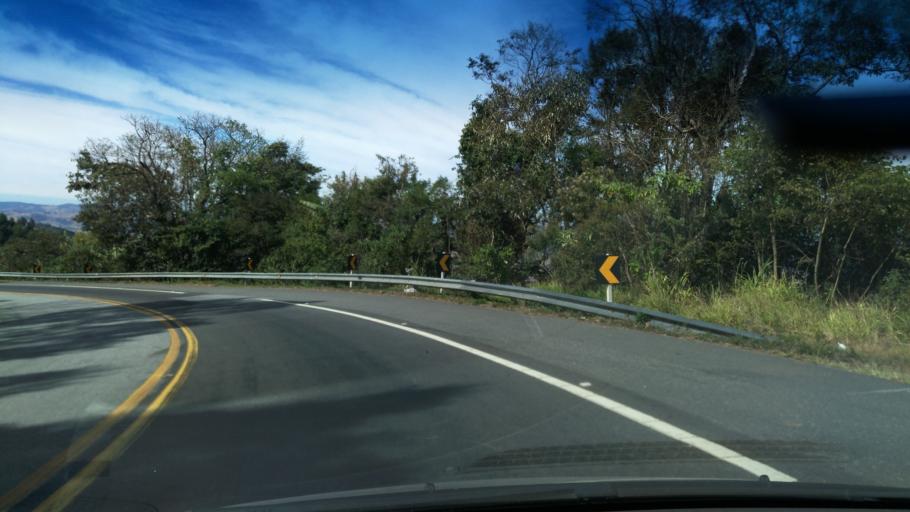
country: BR
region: Minas Gerais
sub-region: Borda Da Mata
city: Borda da Mata
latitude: -22.1326
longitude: -46.1774
